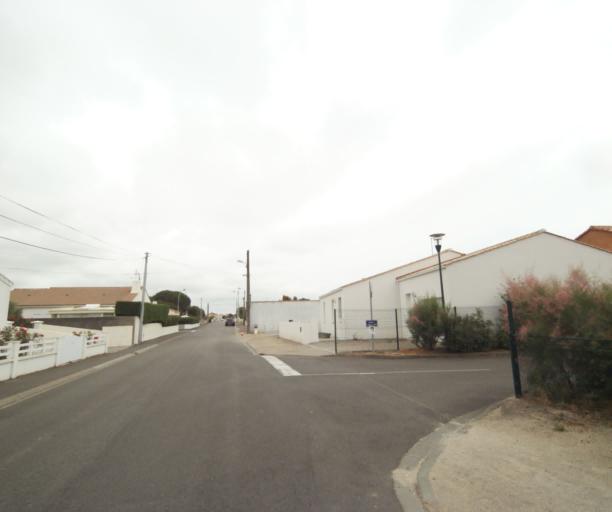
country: FR
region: Pays de la Loire
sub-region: Departement de la Vendee
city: Chateau-d'Olonne
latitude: 46.5004
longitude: -1.7487
